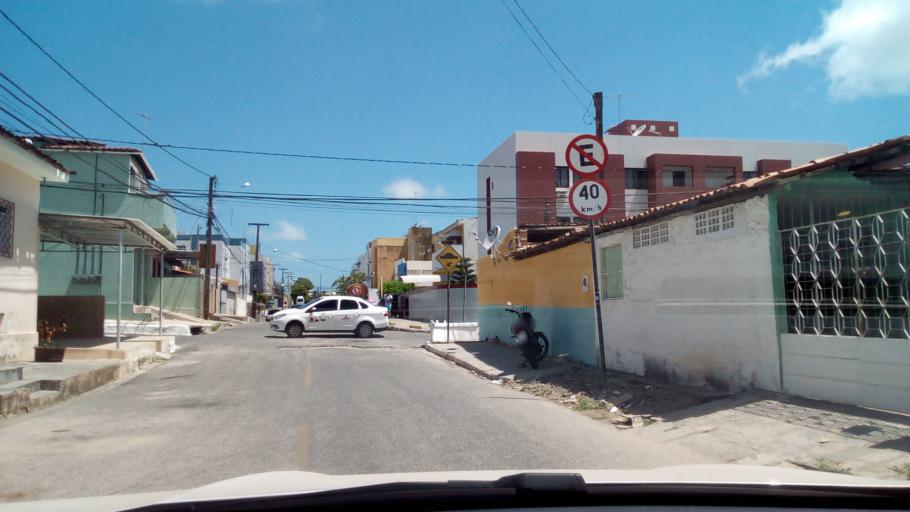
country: BR
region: Paraiba
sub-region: Joao Pessoa
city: Joao Pessoa
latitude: -7.1502
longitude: -34.8469
